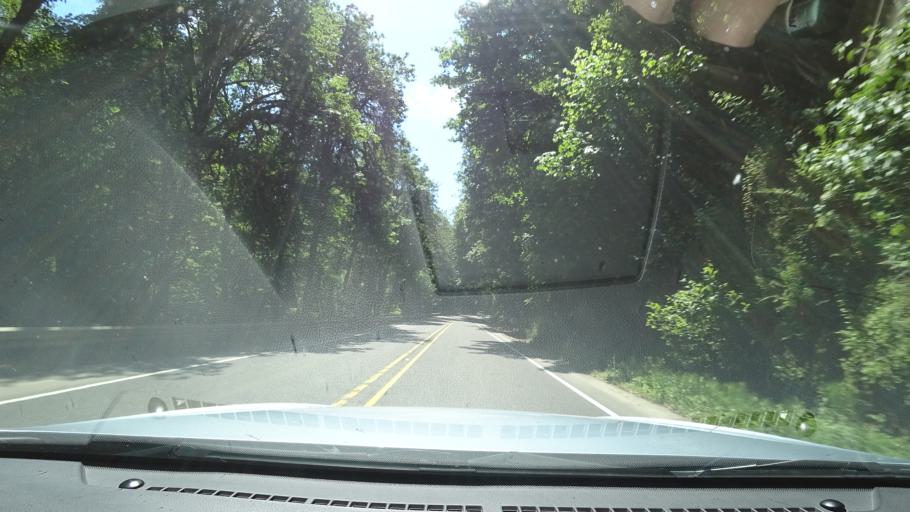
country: US
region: Oregon
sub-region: Lane County
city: Veneta
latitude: 44.0091
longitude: -123.7171
